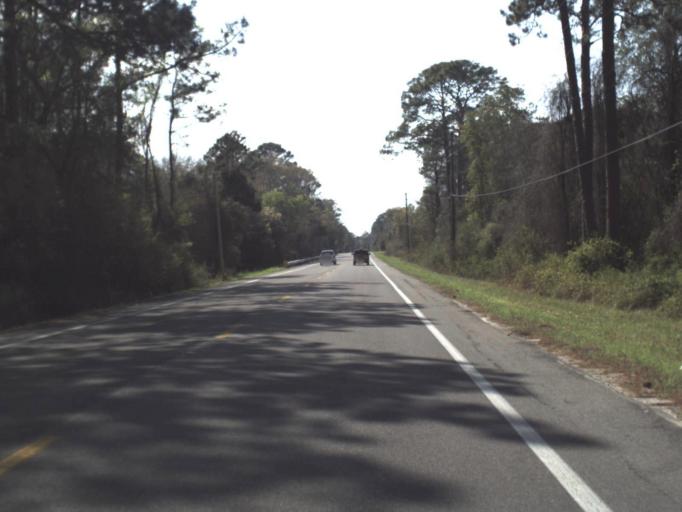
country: US
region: Florida
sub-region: Wakulla County
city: Crawfordville
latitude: 30.0767
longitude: -84.4216
